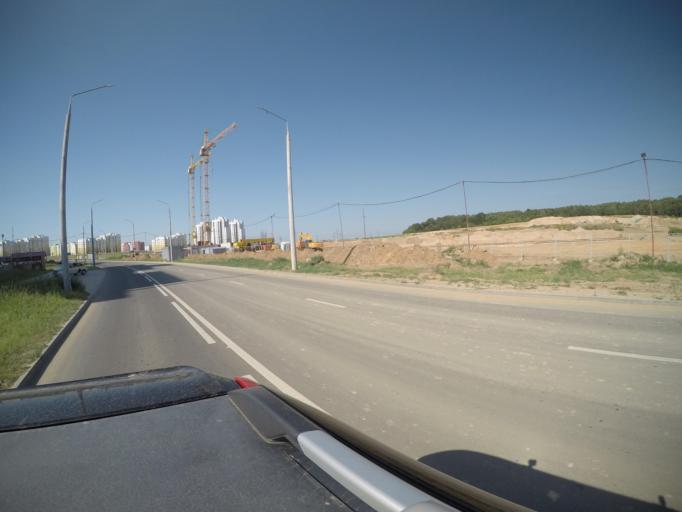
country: BY
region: Grodnenskaya
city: Hrodna
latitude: 53.7225
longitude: 23.8737
